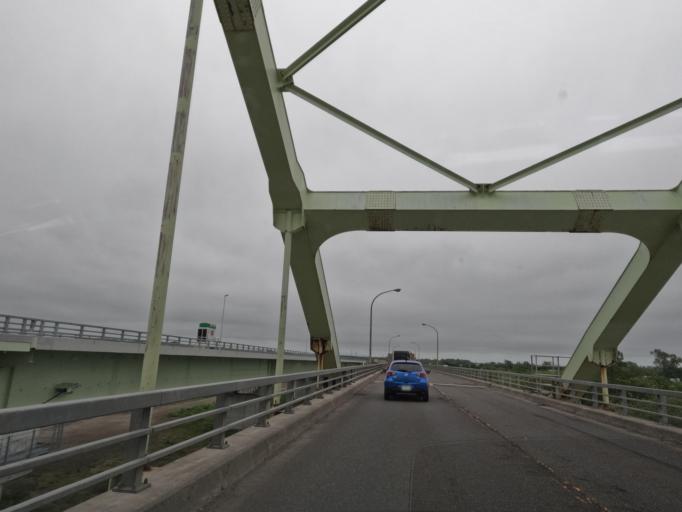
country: JP
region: Hokkaido
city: Ebetsu
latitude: 43.1367
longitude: 141.5124
